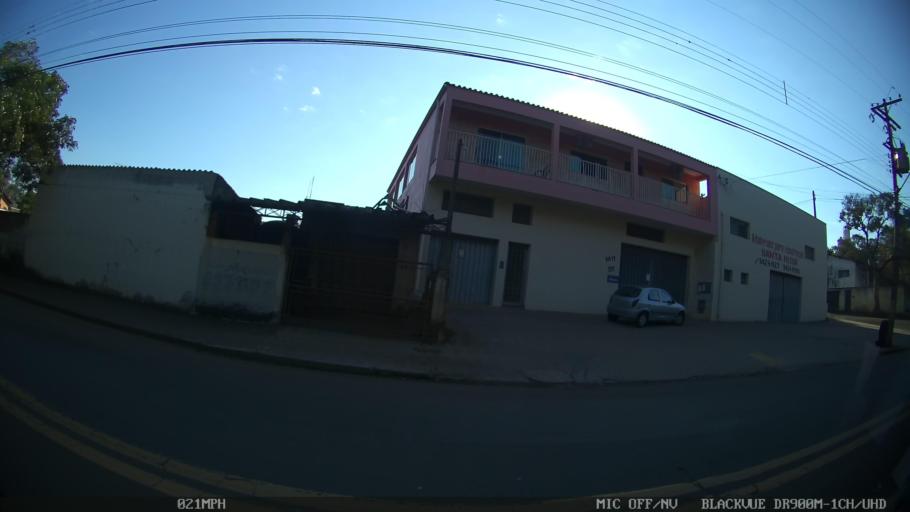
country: BR
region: Sao Paulo
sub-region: Piracicaba
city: Piracicaba
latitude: -22.6809
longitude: -47.6341
